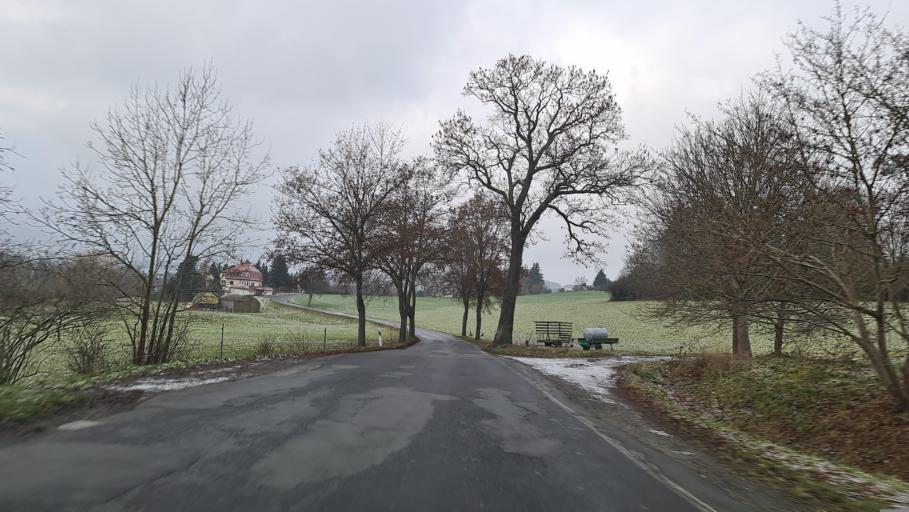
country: DE
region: Saxony
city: Weischlitz
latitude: 50.4581
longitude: 12.0644
